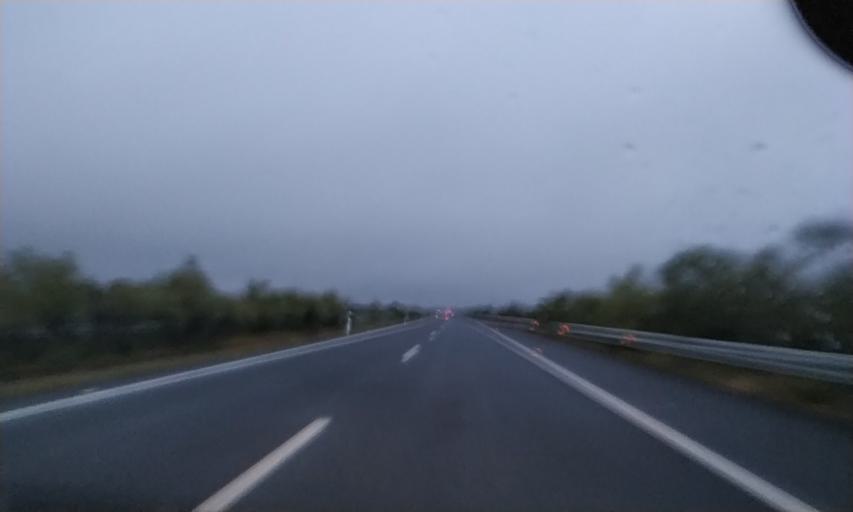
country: ES
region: Extremadura
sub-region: Provincia de Badajoz
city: Carmonita
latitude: 39.1095
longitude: -6.2809
